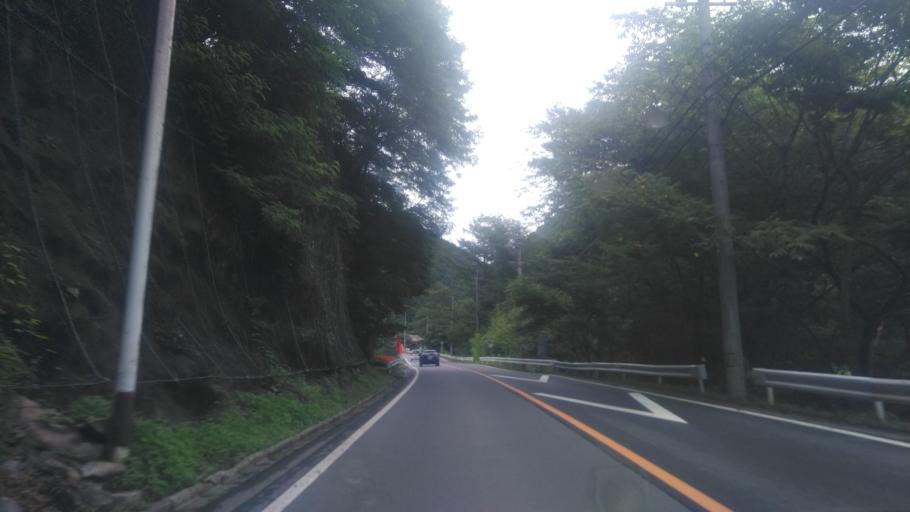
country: JP
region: Nagano
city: Ueda
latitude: 36.4809
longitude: 138.3509
